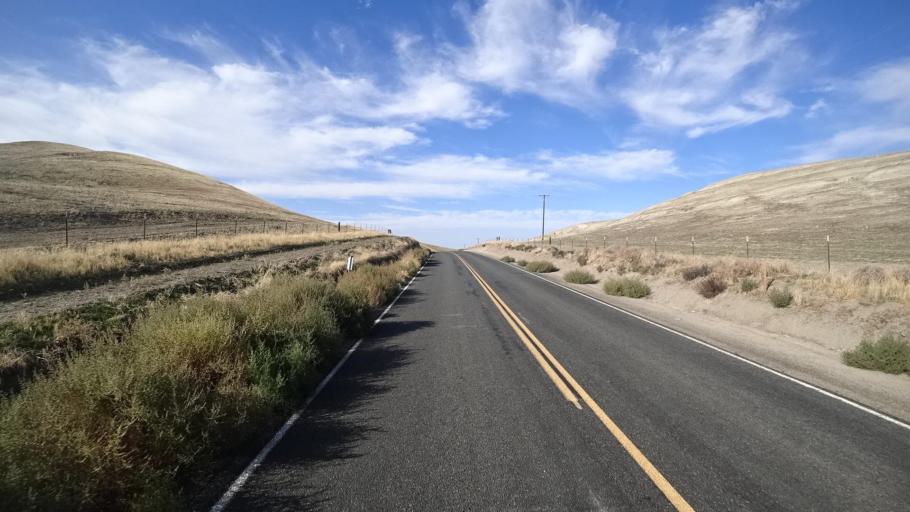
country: US
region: California
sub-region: Kern County
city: Oildale
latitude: 35.6097
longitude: -118.9015
